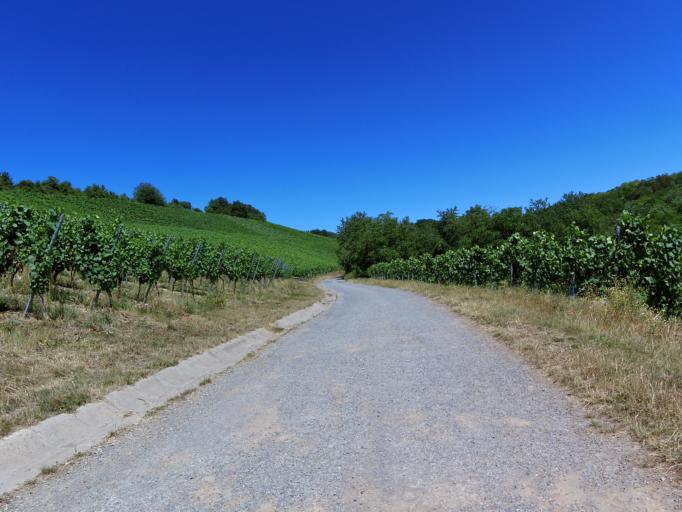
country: DE
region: Bavaria
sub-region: Regierungsbezirk Unterfranken
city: Gerbrunn
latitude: 49.7586
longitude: 10.0037
